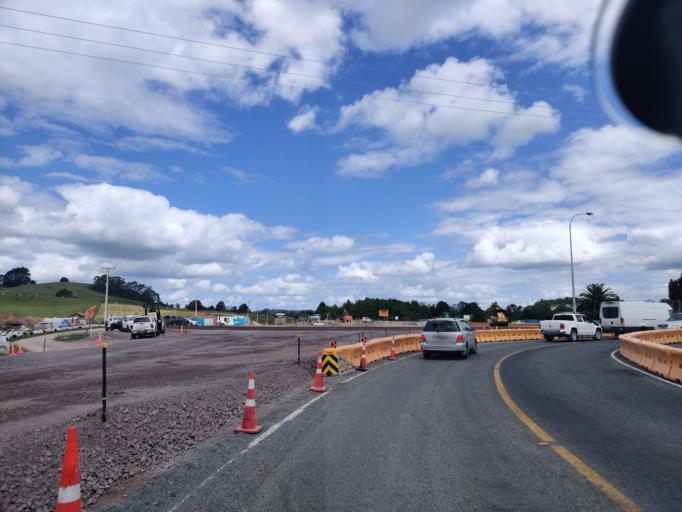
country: NZ
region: Northland
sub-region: Far North District
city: Kerikeri
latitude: -35.3026
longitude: 173.9622
